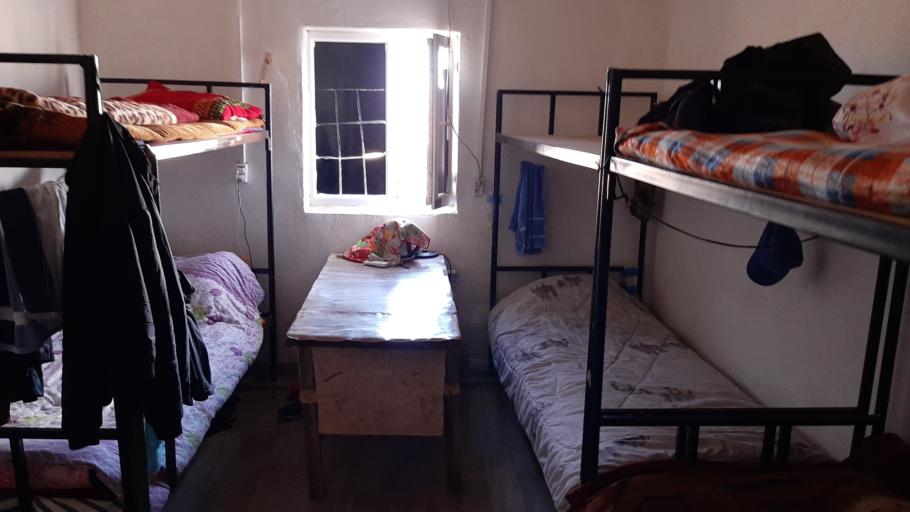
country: KZ
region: Almaty Oblysy
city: Ulken
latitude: 45.1623
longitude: 73.9411
